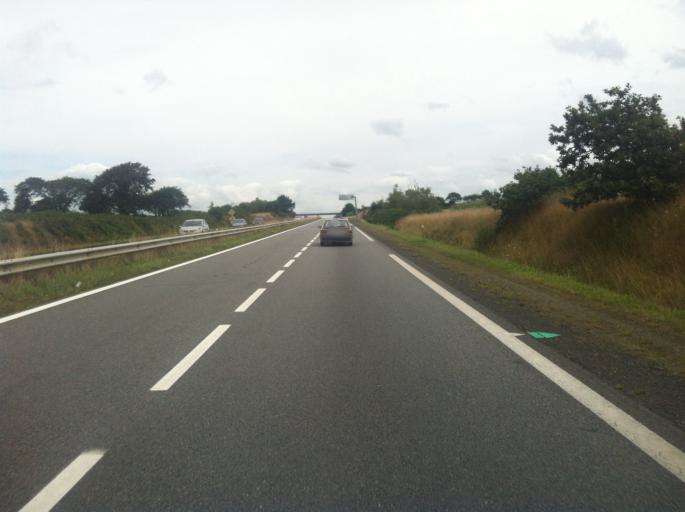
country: FR
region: Brittany
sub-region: Departement du Finistere
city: Kersaint-Plabennec
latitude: 48.4555
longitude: -4.3698
